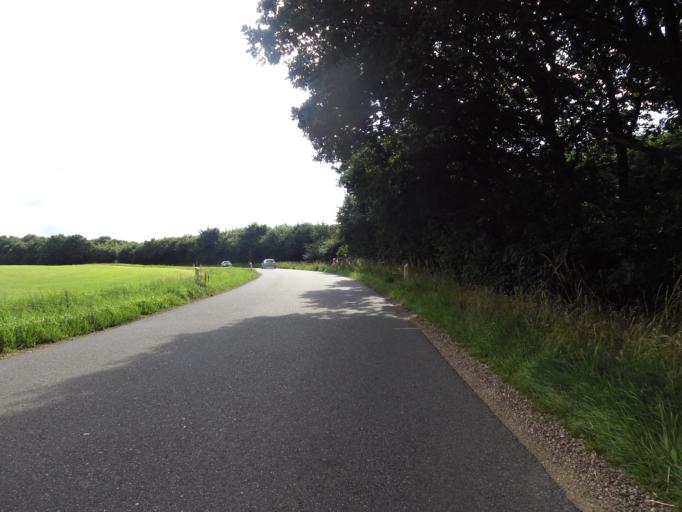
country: DK
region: South Denmark
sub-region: Haderslev Kommune
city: Haderslev
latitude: 55.2267
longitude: 9.4500
